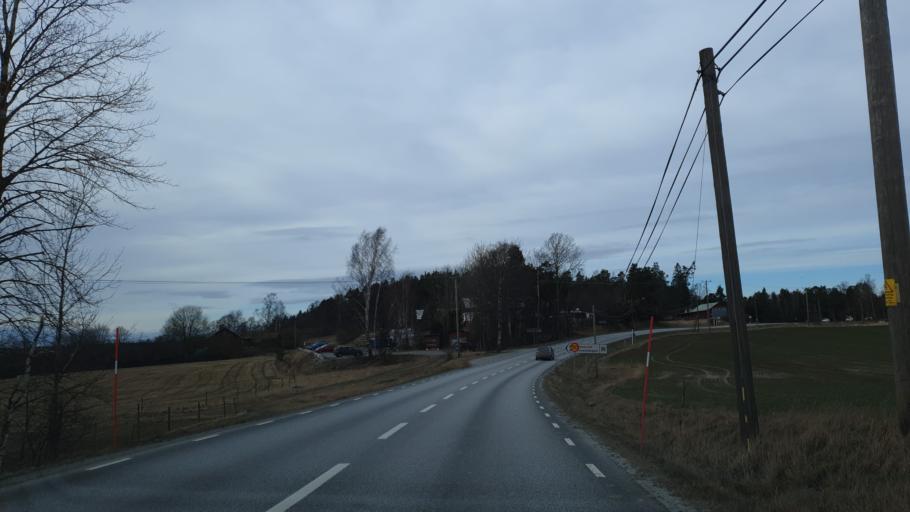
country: SE
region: Stockholm
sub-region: Vallentuna Kommun
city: Vallentuna
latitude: 59.5398
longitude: 18.1706
